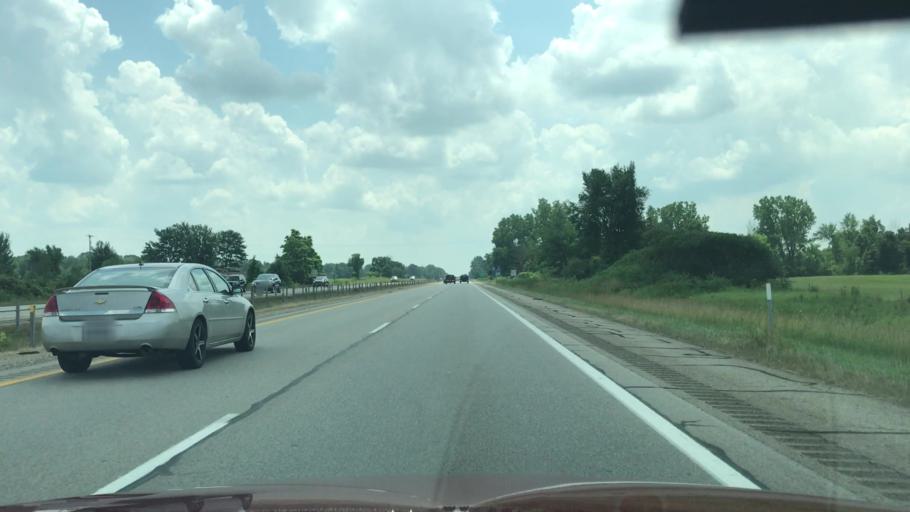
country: US
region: Michigan
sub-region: Allegan County
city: Wayland
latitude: 42.6981
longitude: -85.6598
